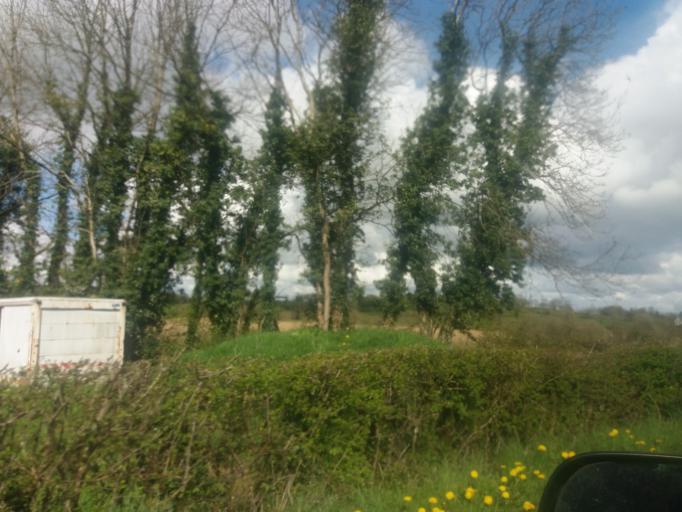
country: IE
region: Ulster
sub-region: An Cabhan
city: Belturbet
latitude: 54.1734
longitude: -7.5049
